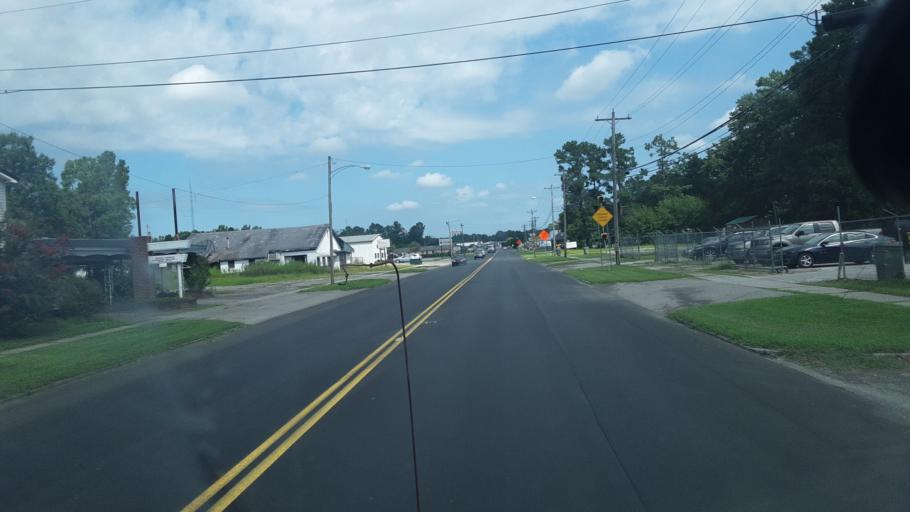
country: US
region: South Carolina
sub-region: Bamberg County
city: Bamberg
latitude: 33.3051
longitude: -81.0337
